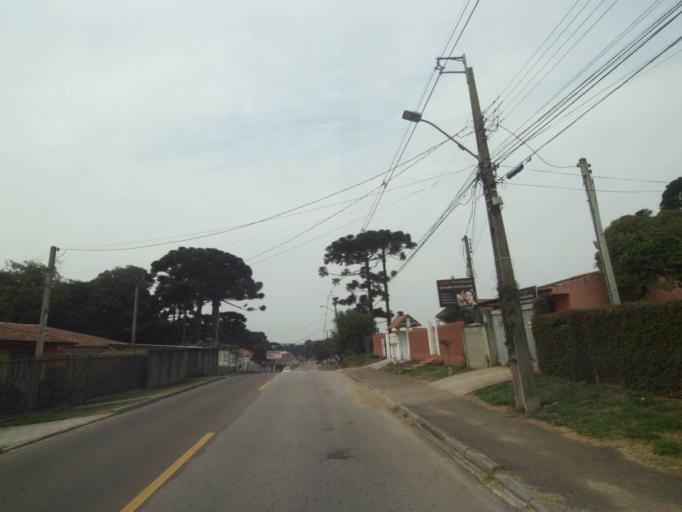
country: BR
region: Parana
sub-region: Sao Jose Dos Pinhais
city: Sao Jose dos Pinhais
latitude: -25.5283
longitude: -49.2819
